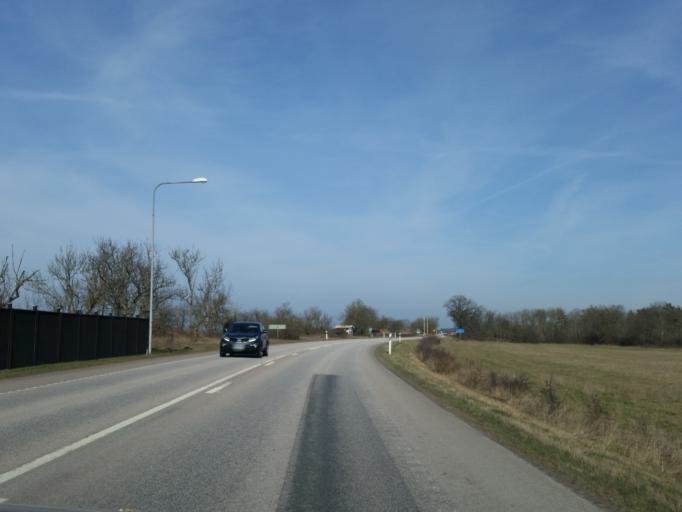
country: SE
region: Kalmar
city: Faerjestaden
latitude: 56.7228
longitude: 16.5362
